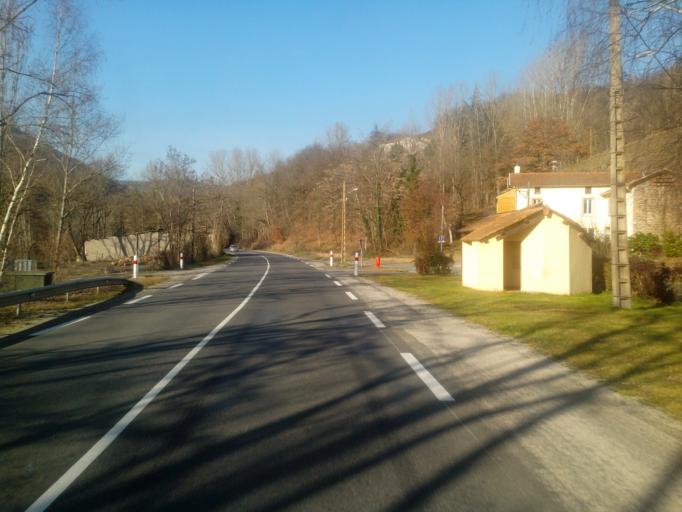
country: FR
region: Midi-Pyrenees
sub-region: Departement de l'Aveyron
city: Viviez
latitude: 44.5652
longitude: 2.2129
